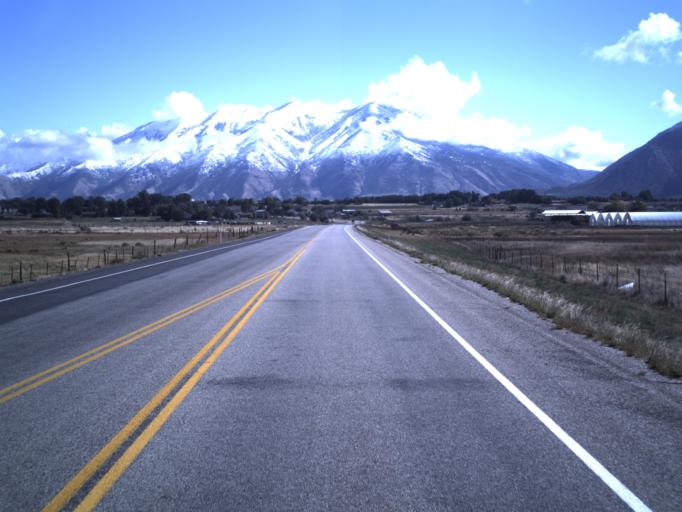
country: US
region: Utah
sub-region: Utah County
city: Salem
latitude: 40.0853
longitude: -111.6847
